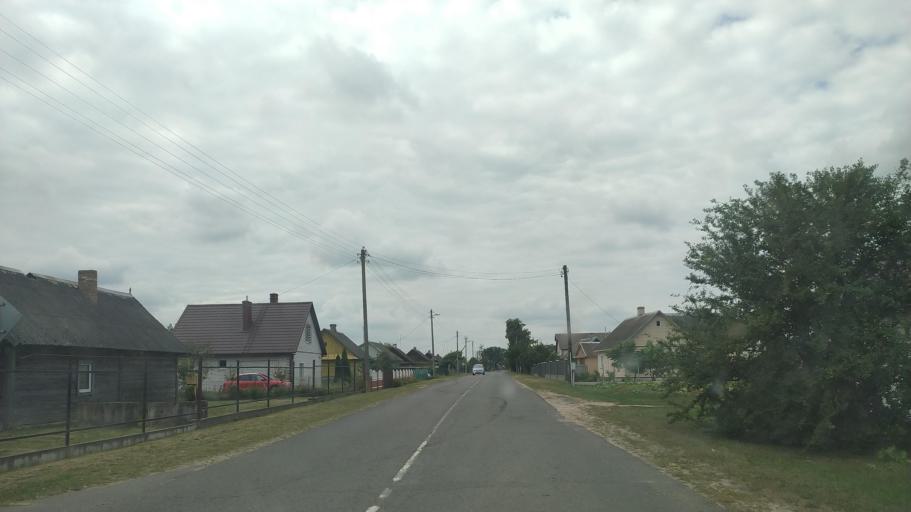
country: BY
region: Brest
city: Byelaazyorsk
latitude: 52.5397
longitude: 25.0971
